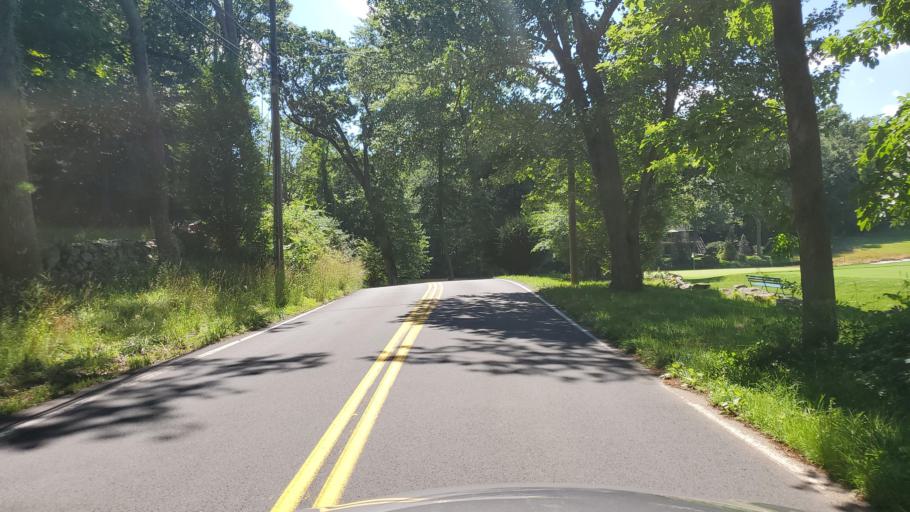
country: US
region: Connecticut
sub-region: Fairfield County
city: Westport
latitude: 41.2205
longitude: -73.3299
